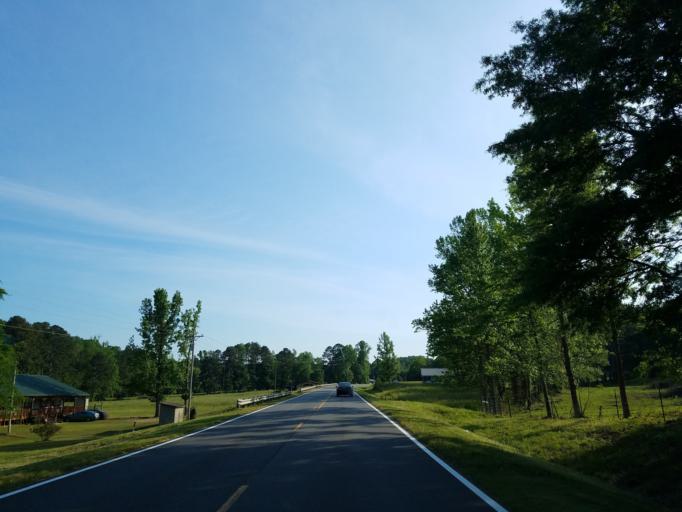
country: US
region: Georgia
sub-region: Chattooga County
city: Trion
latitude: 34.5554
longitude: -85.1907
